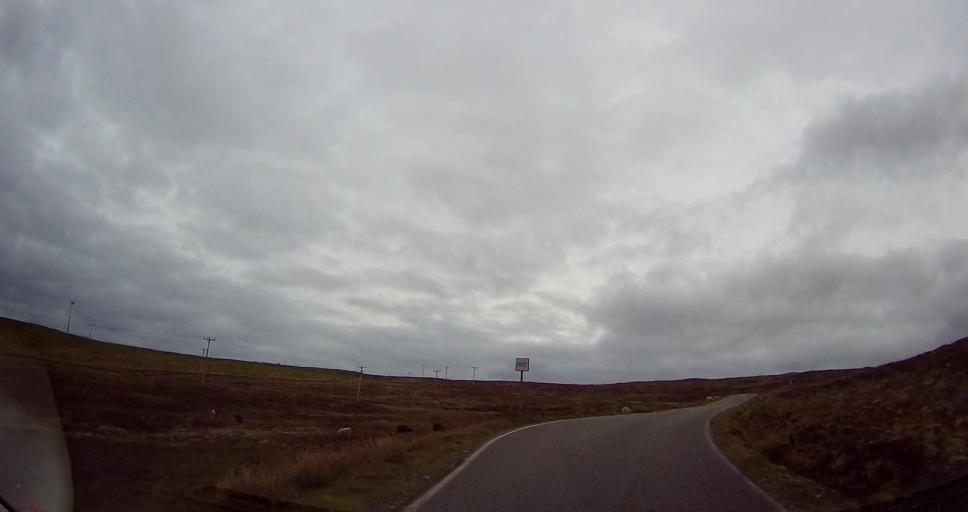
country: GB
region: Scotland
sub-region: Shetland Islands
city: Shetland
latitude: 60.5474
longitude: -1.0605
